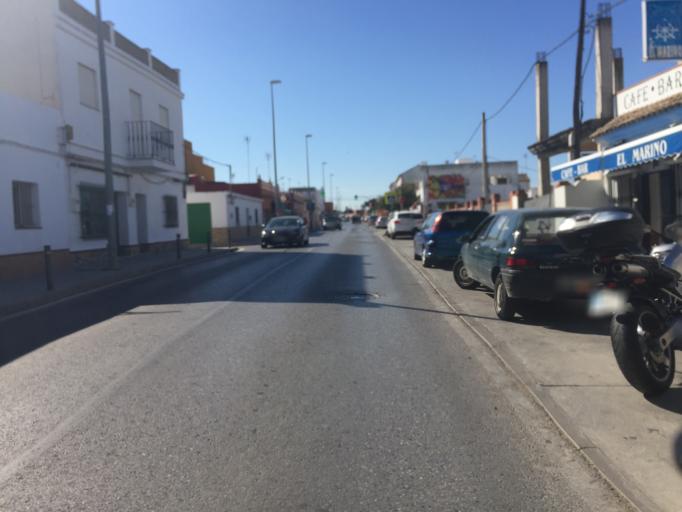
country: ES
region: Andalusia
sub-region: Provincia de Cadiz
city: Chiclana de la Frontera
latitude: 36.4111
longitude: -6.1663
